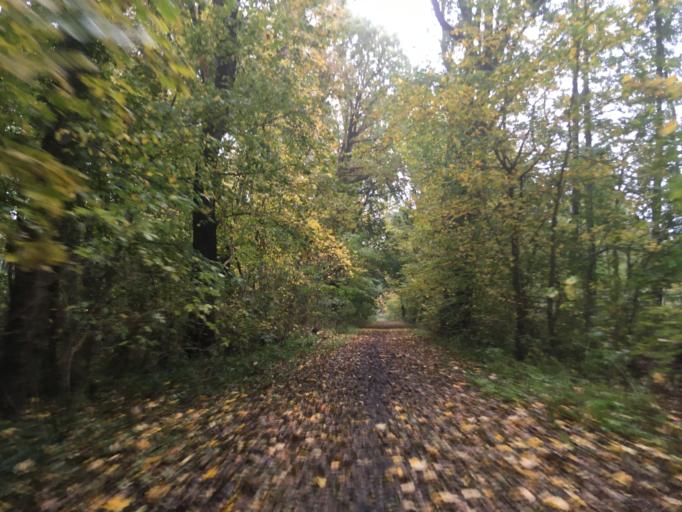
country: DE
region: Brandenburg
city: Neu Zauche
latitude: 52.0368
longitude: 14.0444
